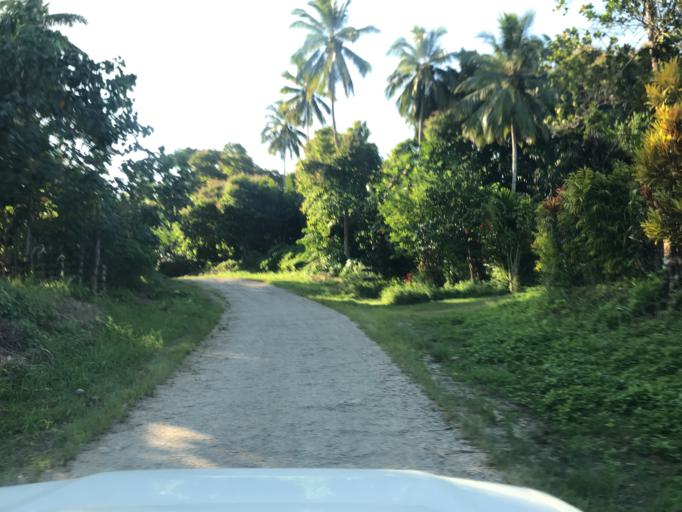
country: VU
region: Sanma
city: Luganville
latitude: -15.5943
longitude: 166.9002
